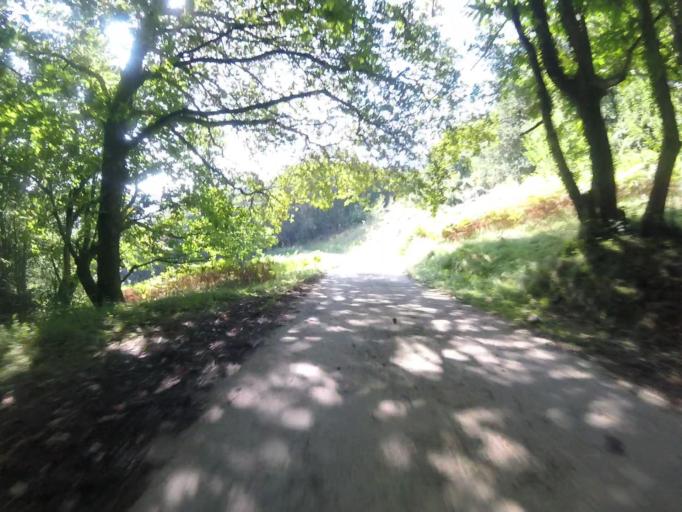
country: ES
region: Basque Country
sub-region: Provincia de Guipuzcoa
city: Irun
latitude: 43.3233
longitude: -1.7516
